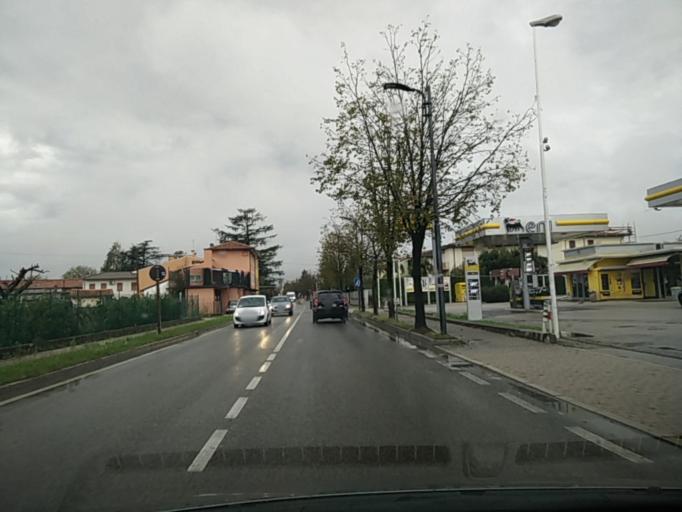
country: IT
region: Veneto
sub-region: Provincia di Vicenza
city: Rosa
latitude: 45.7233
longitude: 11.7697
